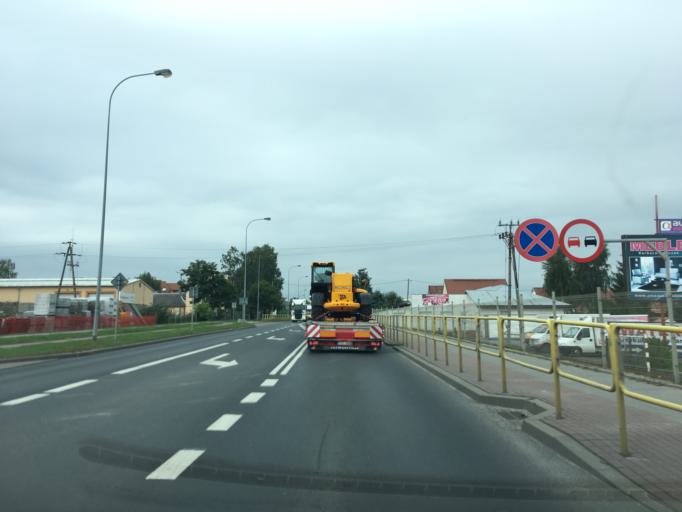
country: PL
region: Warmian-Masurian Voivodeship
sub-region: Powiat ostrodzki
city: Ostroda
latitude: 53.6907
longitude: 19.9816
